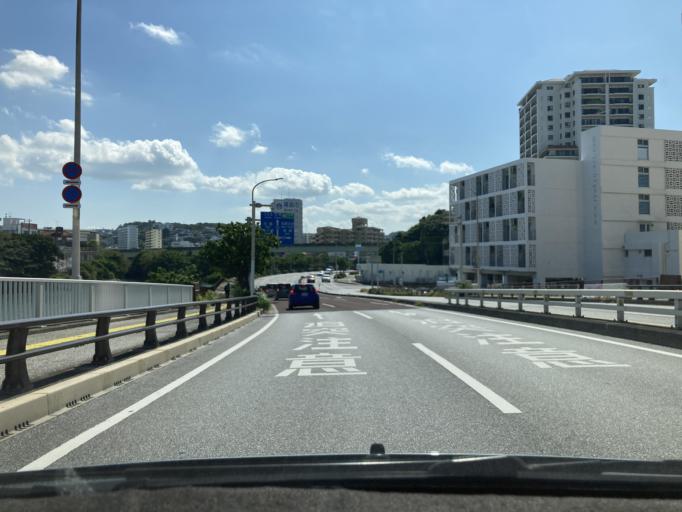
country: JP
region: Okinawa
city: Ginowan
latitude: 26.2696
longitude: 127.7260
